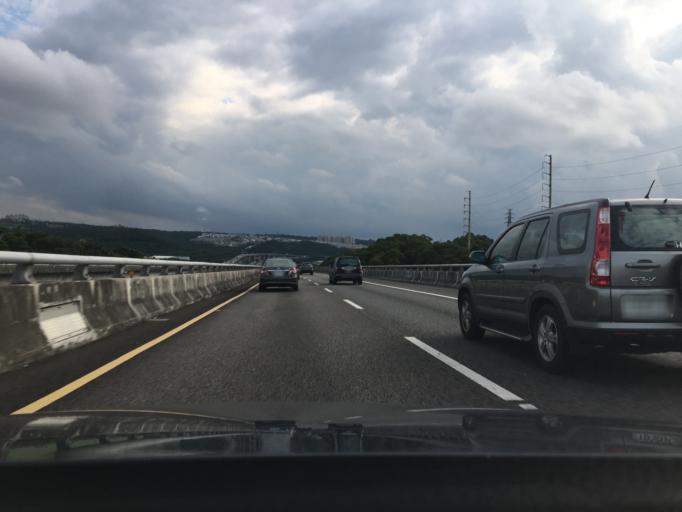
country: TW
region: Taiwan
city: Daxi
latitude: 24.9217
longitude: 121.1687
